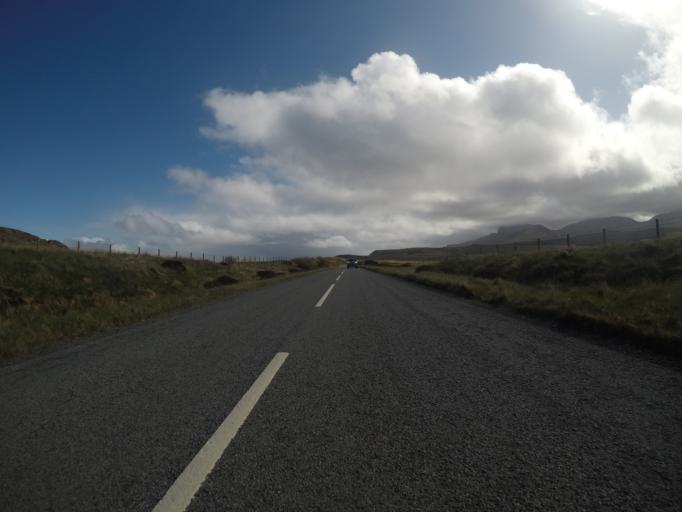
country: GB
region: Scotland
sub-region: Highland
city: Portree
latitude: 57.5708
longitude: -6.1527
